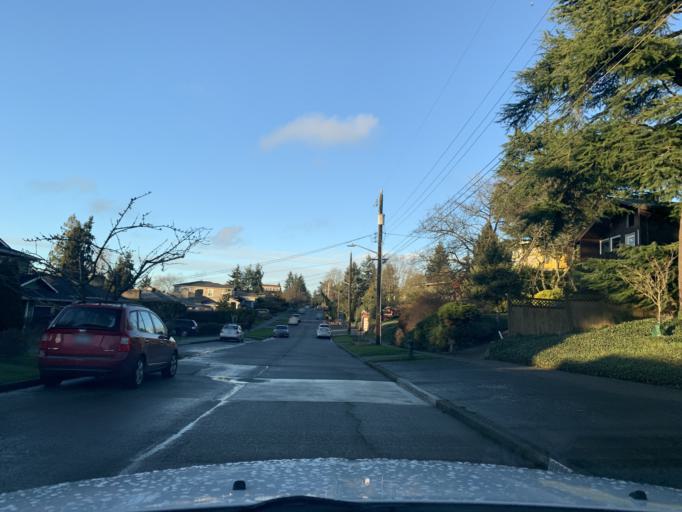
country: US
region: Washington
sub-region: King County
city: Shoreline
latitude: 47.6912
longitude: -122.3270
